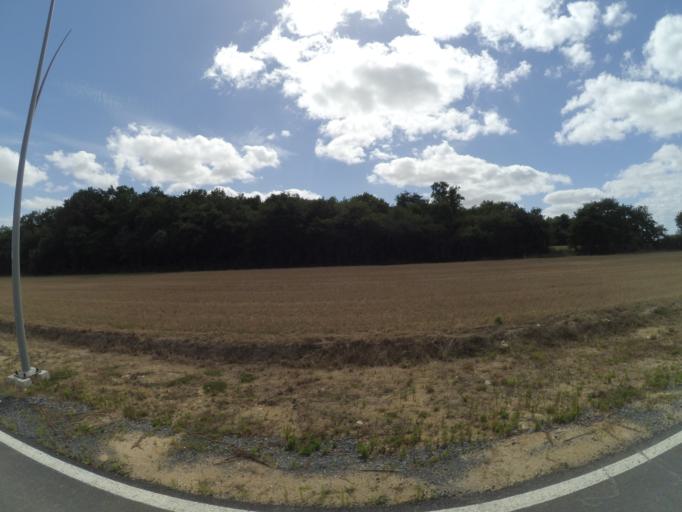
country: FR
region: Pays de la Loire
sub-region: Departement de la Vendee
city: Saint-Hilaire-de-Loulay
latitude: 47.0176
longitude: -1.3467
